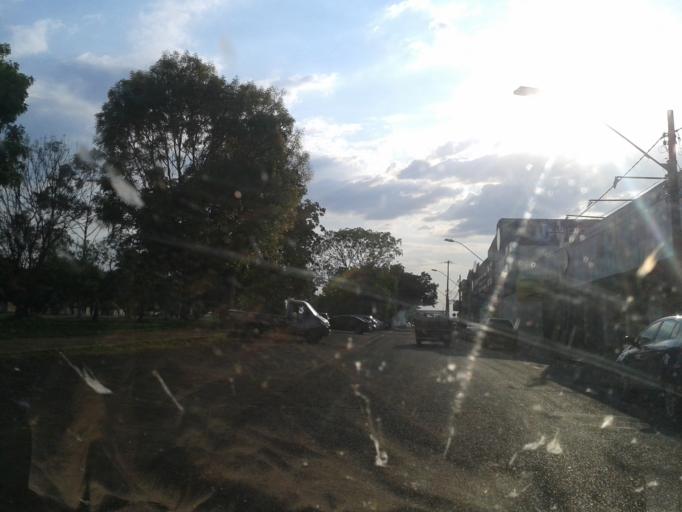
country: BR
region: Minas Gerais
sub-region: Uberlandia
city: Uberlandia
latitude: -18.9392
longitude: -48.3093
